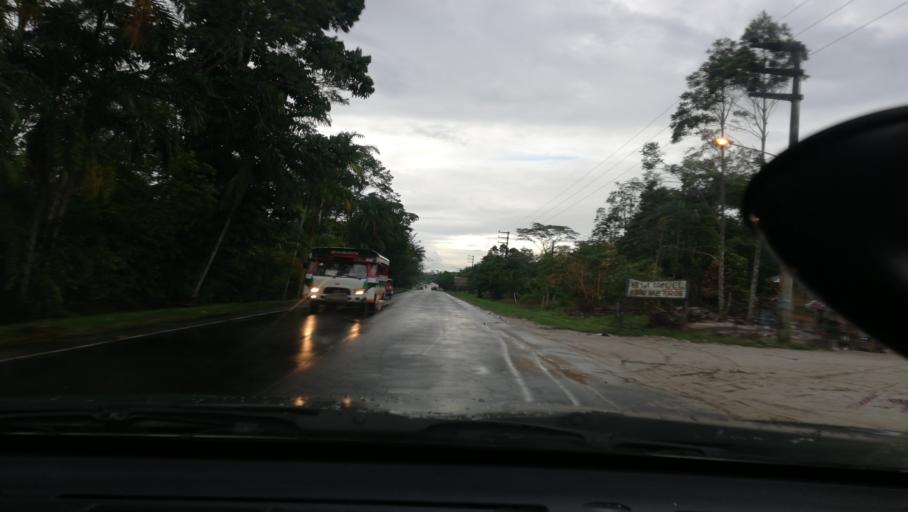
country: PE
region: Loreto
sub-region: Provincia de Maynas
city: Iquitos
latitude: -3.8915
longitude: -73.3506
